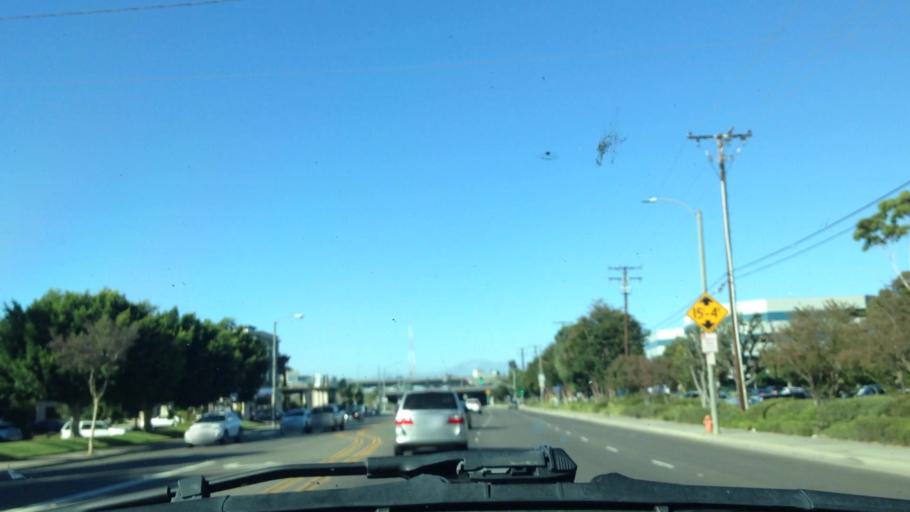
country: US
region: California
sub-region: Orange County
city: Santa Ana
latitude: 33.7758
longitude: -117.8902
